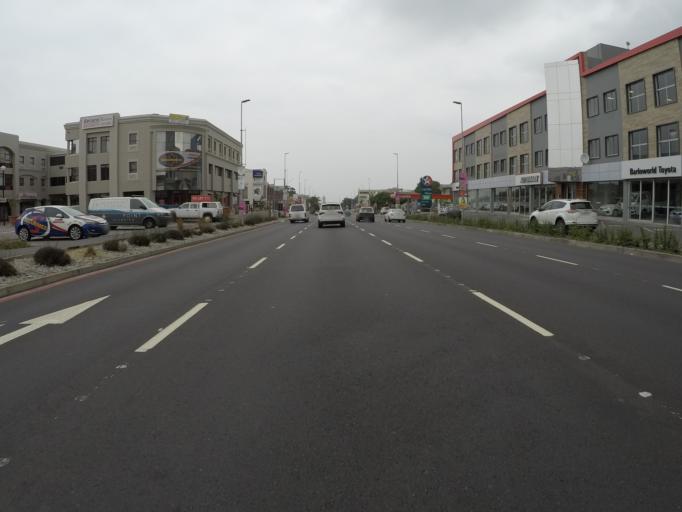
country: ZA
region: Western Cape
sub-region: City of Cape Town
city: Kraaifontein
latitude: -33.8815
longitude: 18.6363
